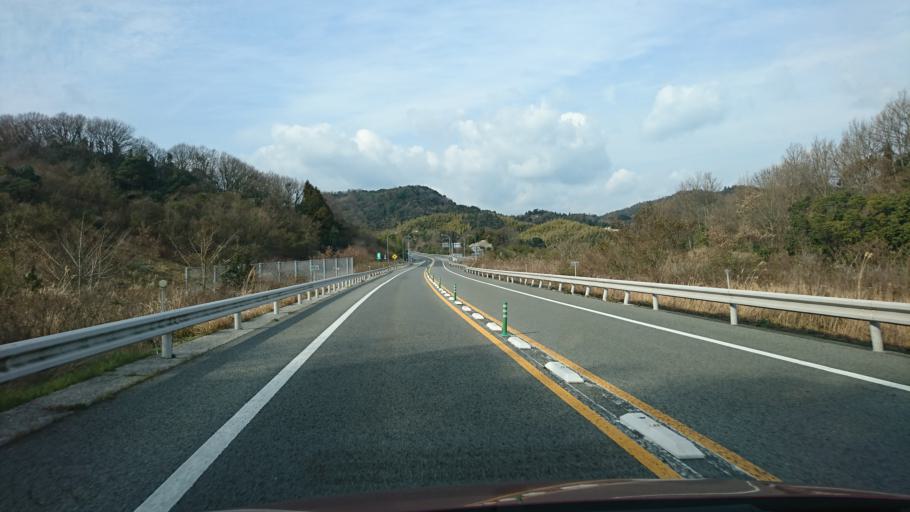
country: JP
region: Hiroshima
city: Innoshima
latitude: 34.1289
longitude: 133.0337
